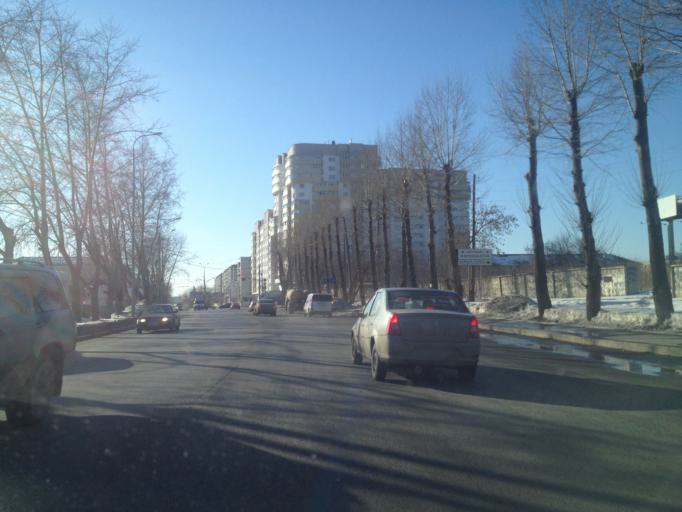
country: RU
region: Sverdlovsk
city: Yekaterinburg
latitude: 56.9145
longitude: 60.6141
